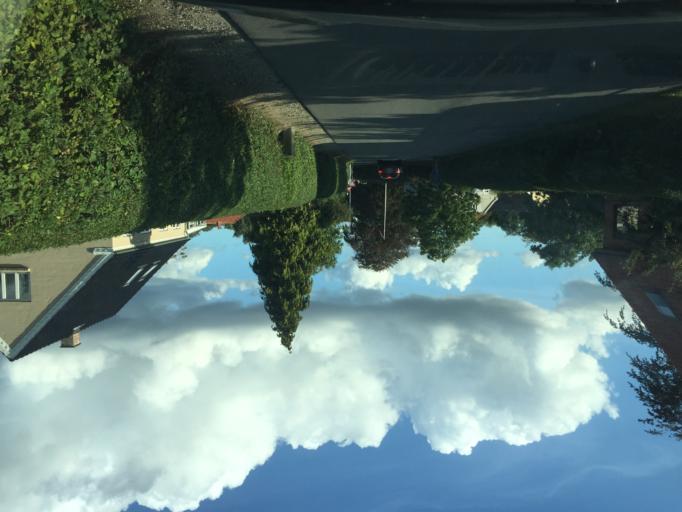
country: DK
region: South Denmark
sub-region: Nyborg Kommune
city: Nyborg
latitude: 55.3064
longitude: 10.7299
